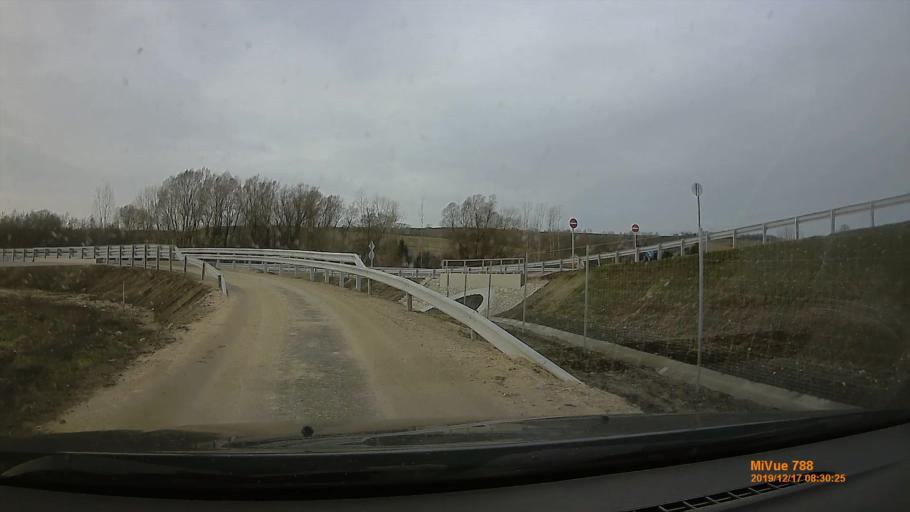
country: HU
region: Somogy
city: Karad
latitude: 46.6669
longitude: 17.7834
